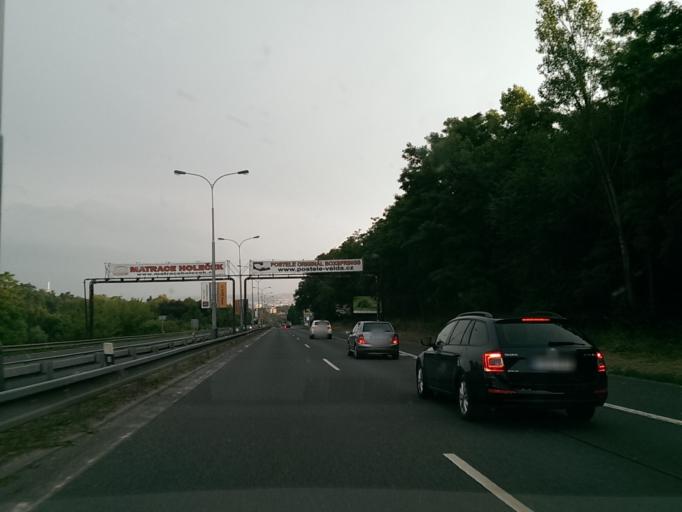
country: CZ
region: Praha
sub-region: Praha 9
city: Strizkov
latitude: 50.1246
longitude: 14.4802
